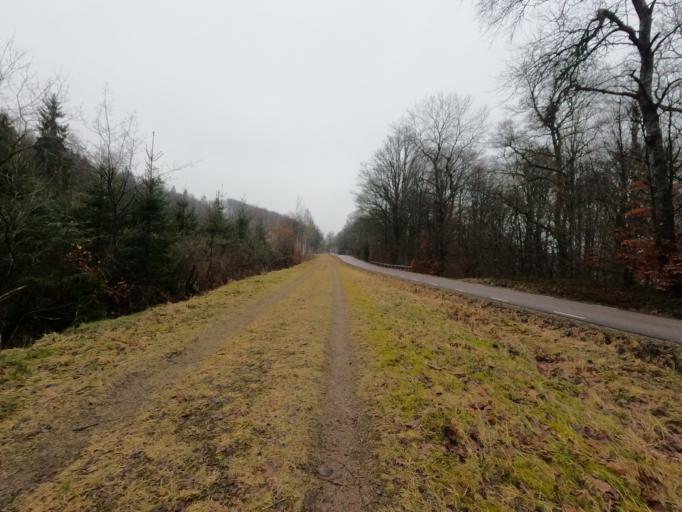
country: SE
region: Halland
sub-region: Halmstads Kommun
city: Oskarstrom
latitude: 56.7552
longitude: 13.1711
